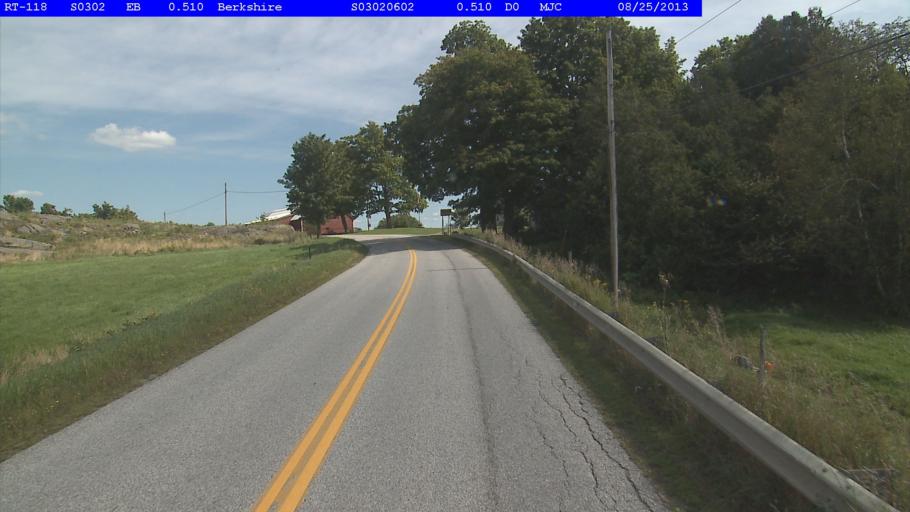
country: US
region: Vermont
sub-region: Franklin County
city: Enosburg Falls
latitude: 44.9844
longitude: -72.8054
